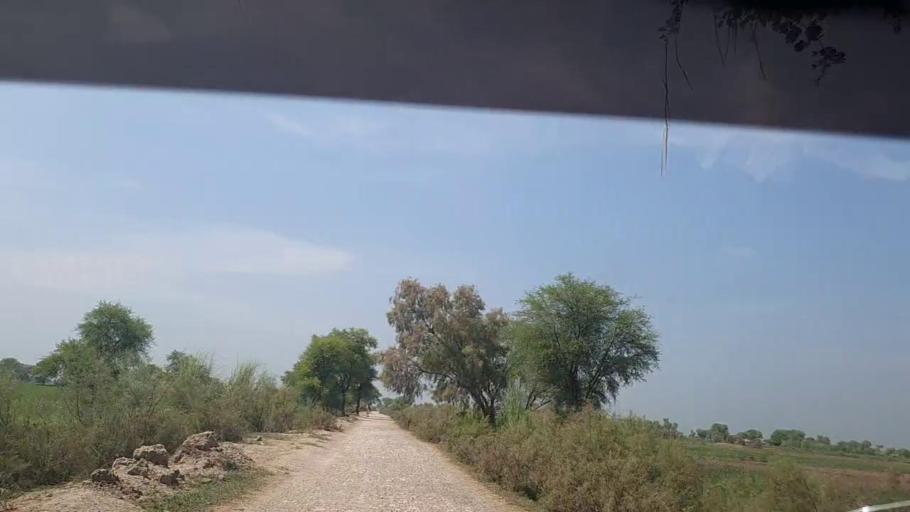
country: PK
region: Sindh
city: Thul
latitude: 28.2066
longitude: 68.6927
